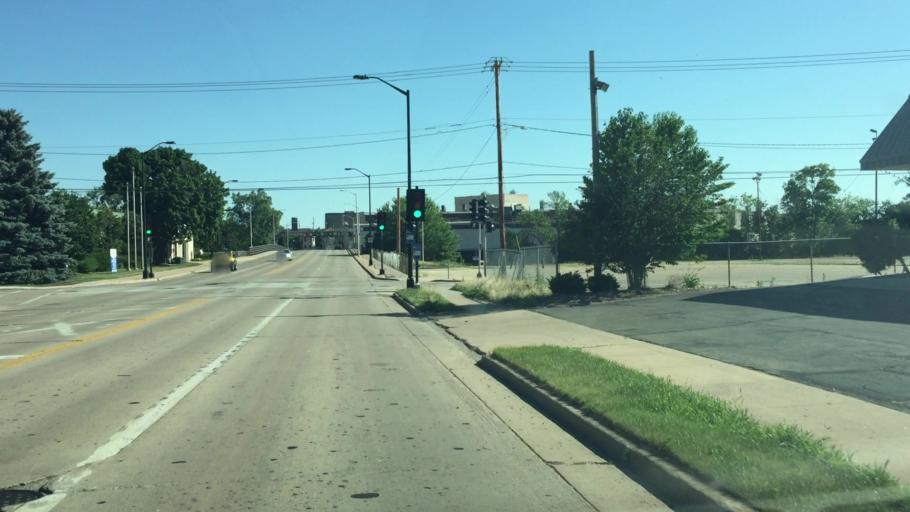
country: US
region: Wisconsin
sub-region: Winnebago County
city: Menasha
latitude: 44.1951
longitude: -88.4540
